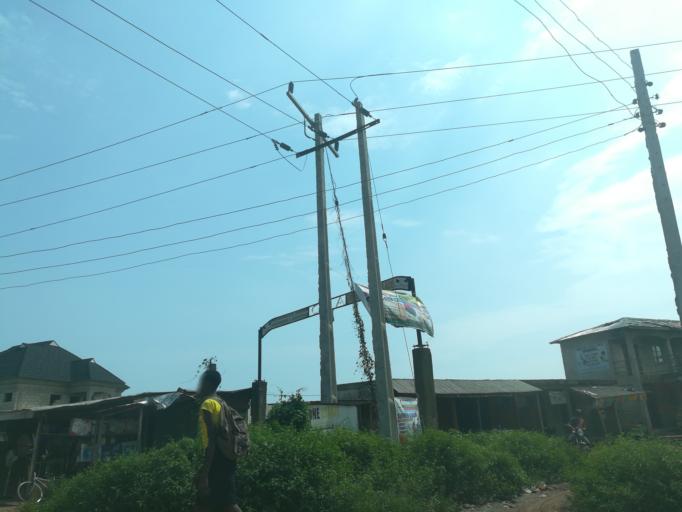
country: NG
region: Lagos
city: Ikorodu
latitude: 6.6004
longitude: 3.6240
